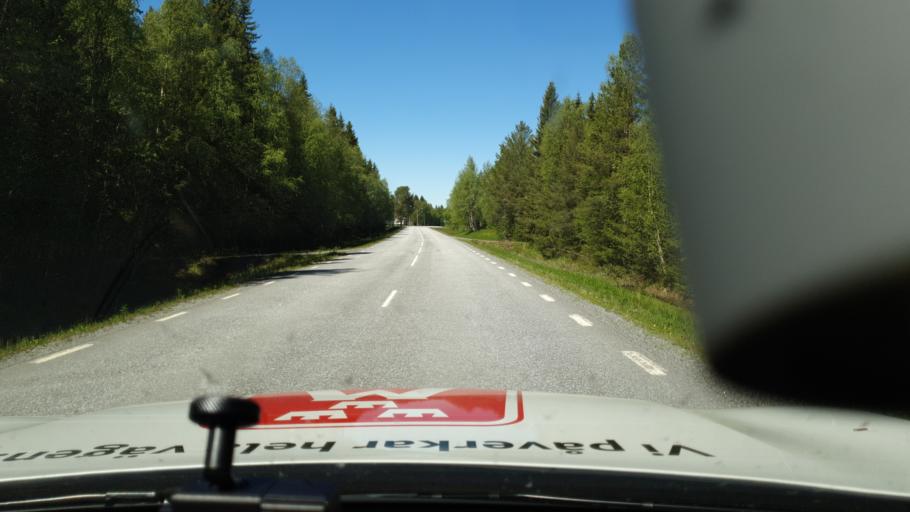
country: SE
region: Vaesterbotten
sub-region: Storumans Kommun
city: Storuman
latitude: 65.1993
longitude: 17.0040
